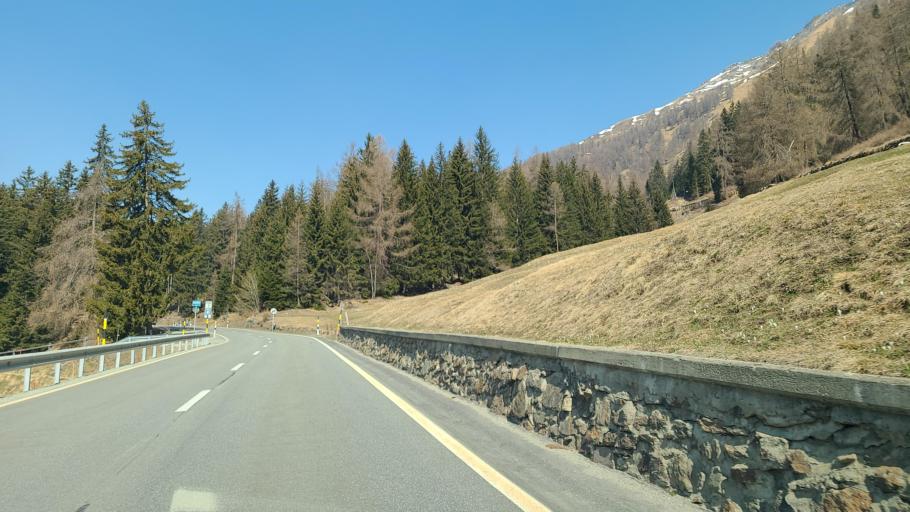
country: CH
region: Grisons
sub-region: Bernina District
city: Poschiavo
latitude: 46.3900
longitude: 10.0792
